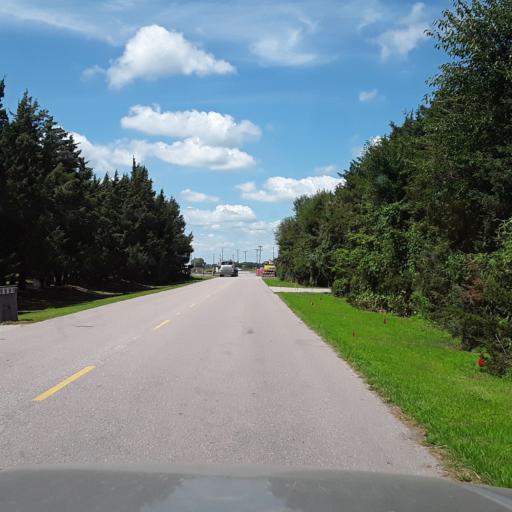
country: US
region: Nebraska
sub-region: Merrick County
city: Central City
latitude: 41.1048
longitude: -98.0167
